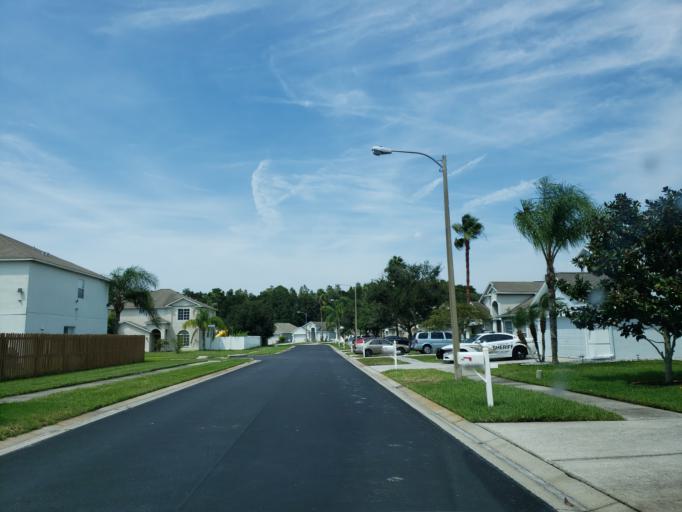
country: US
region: Florida
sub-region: Pasco County
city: Land O' Lakes
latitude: 28.2276
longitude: -82.3940
